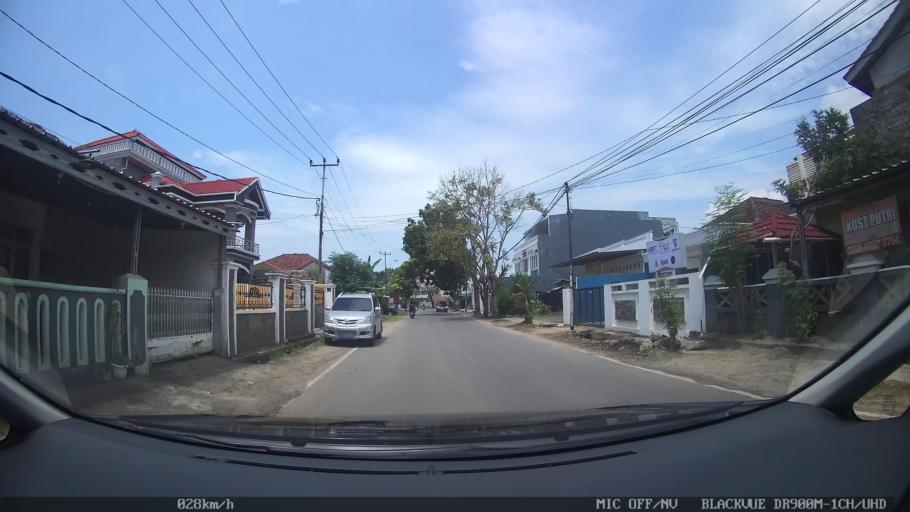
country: ID
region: Lampung
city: Kedaton
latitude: -5.3730
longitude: 105.3006
